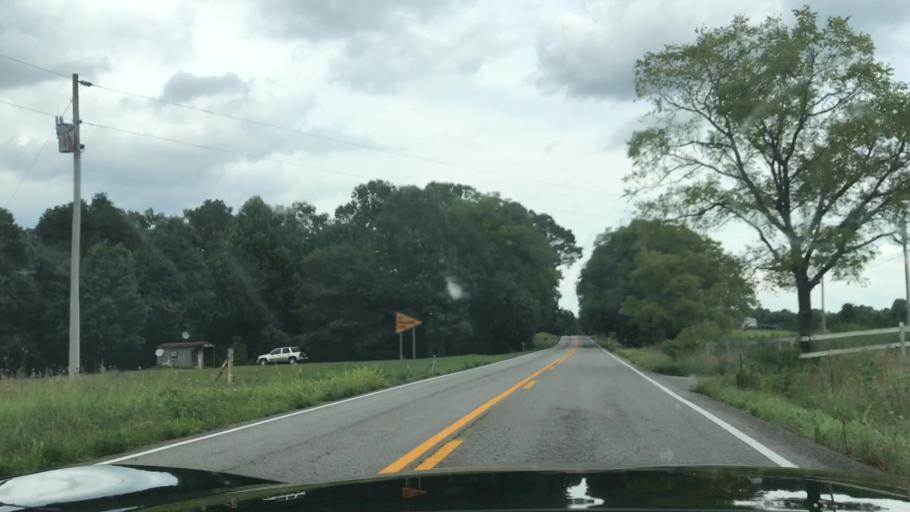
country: US
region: Kentucky
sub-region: Muhlenberg County
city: Central City
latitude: 37.2046
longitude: -86.9478
